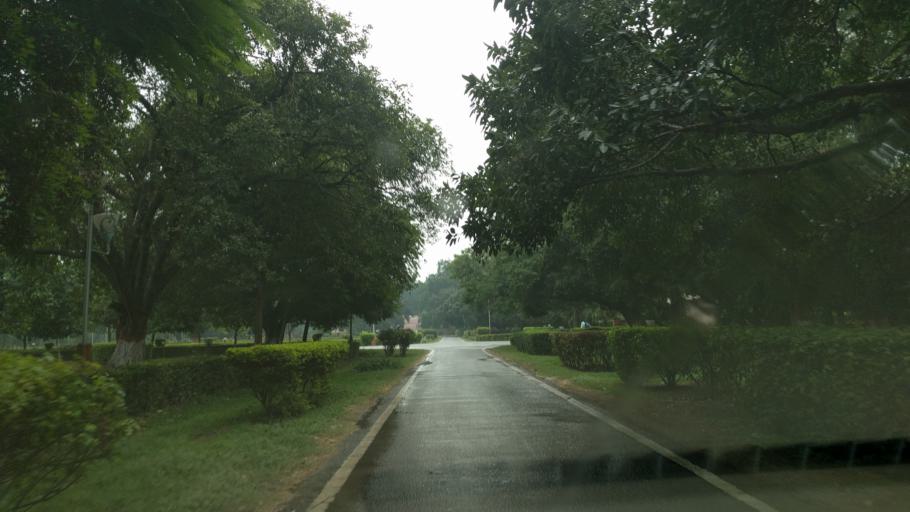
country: IN
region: NCT
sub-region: Central Delhi
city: Karol Bagh
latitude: 28.6389
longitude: 77.1655
